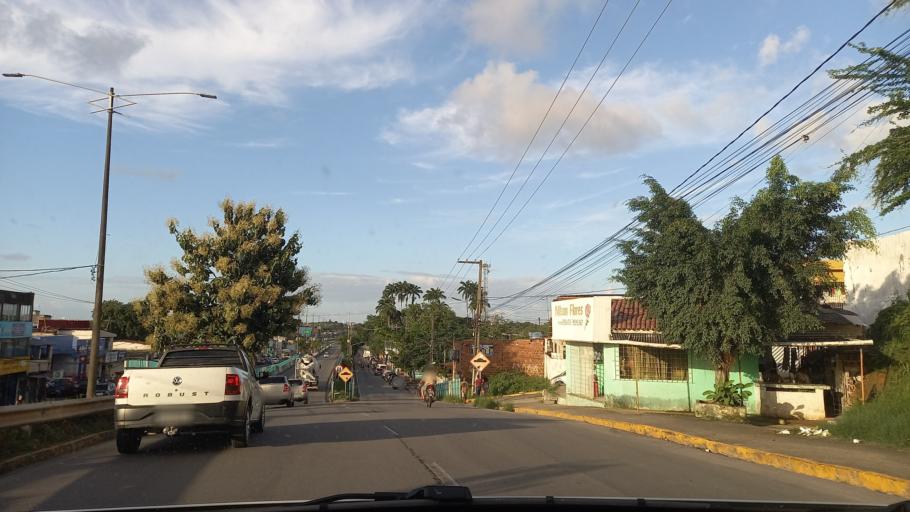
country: BR
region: Pernambuco
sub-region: Jaboatao Dos Guararapes
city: Jaboatao
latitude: -8.2375
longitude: -34.9827
